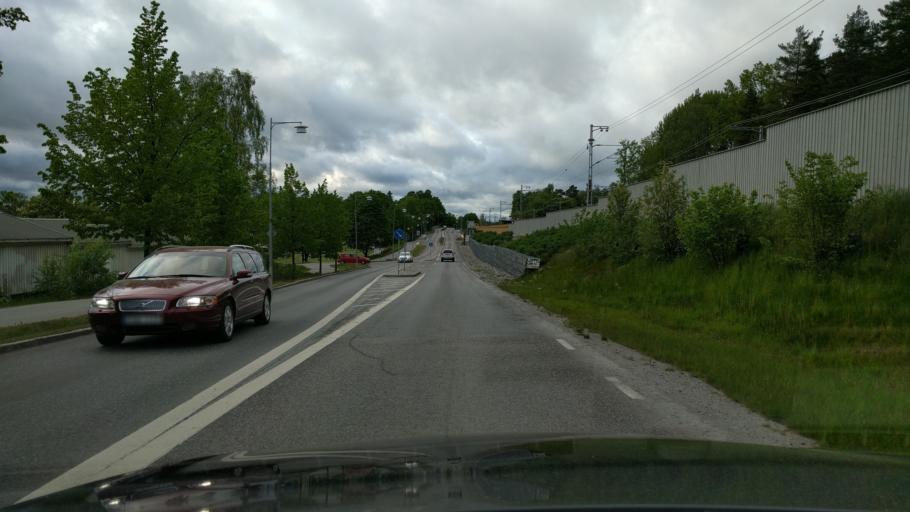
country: SE
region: Stockholm
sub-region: Vallentuna Kommun
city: Vallentuna
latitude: 59.5207
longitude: 18.0730
